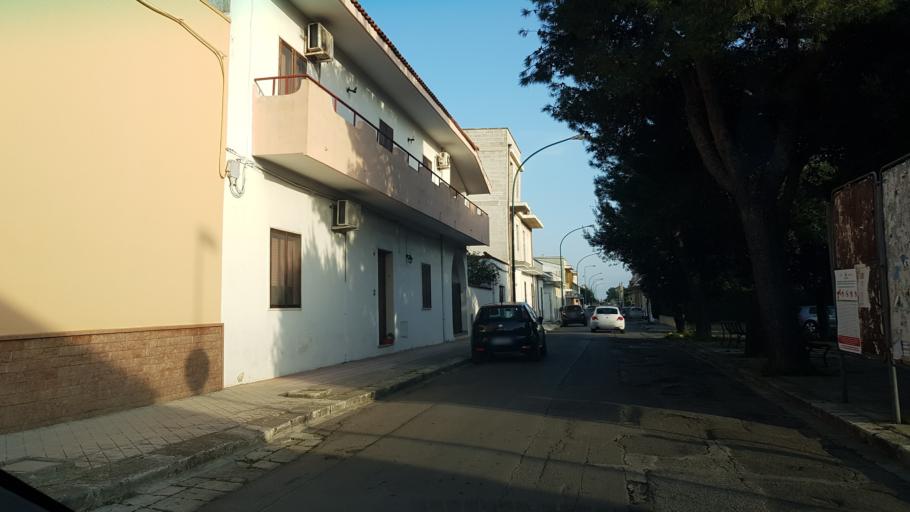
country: IT
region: Apulia
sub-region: Provincia di Lecce
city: Campi Salentina
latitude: 40.3945
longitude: 18.0217
